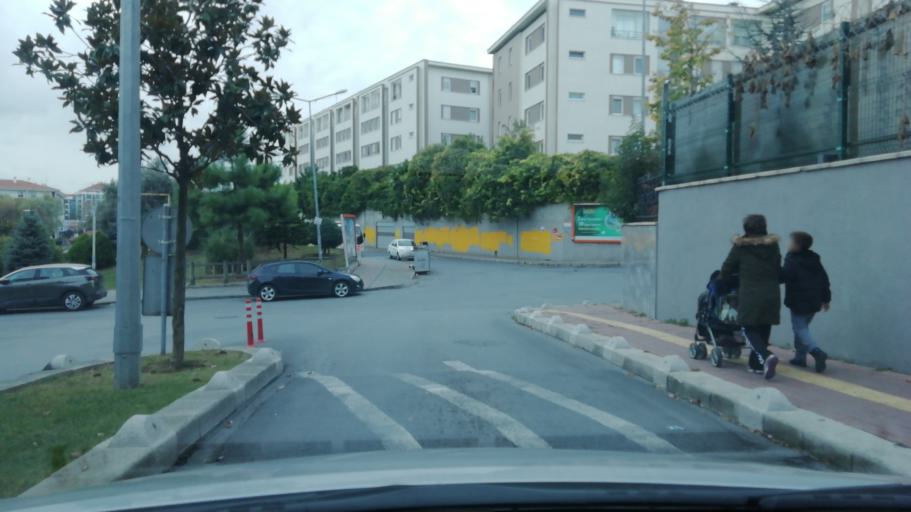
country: TR
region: Istanbul
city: Bahcelievler
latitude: 41.0180
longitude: 28.8291
